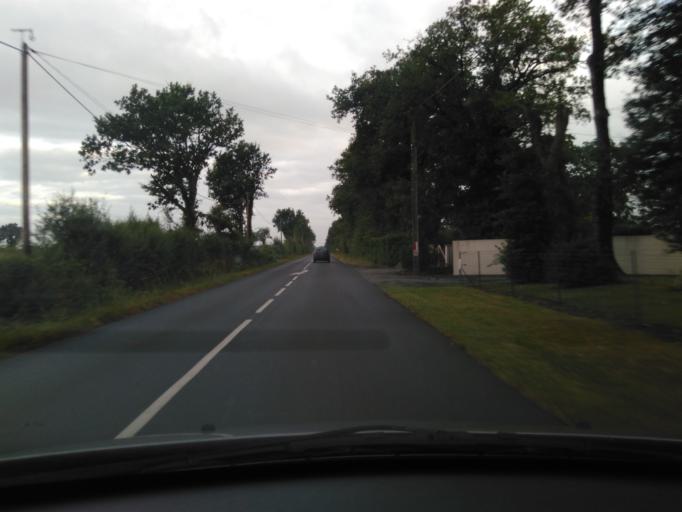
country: FR
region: Pays de la Loire
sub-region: Departement de la Vendee
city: Dompierre-sur-Yon
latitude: 46.7290
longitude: -1.3622
